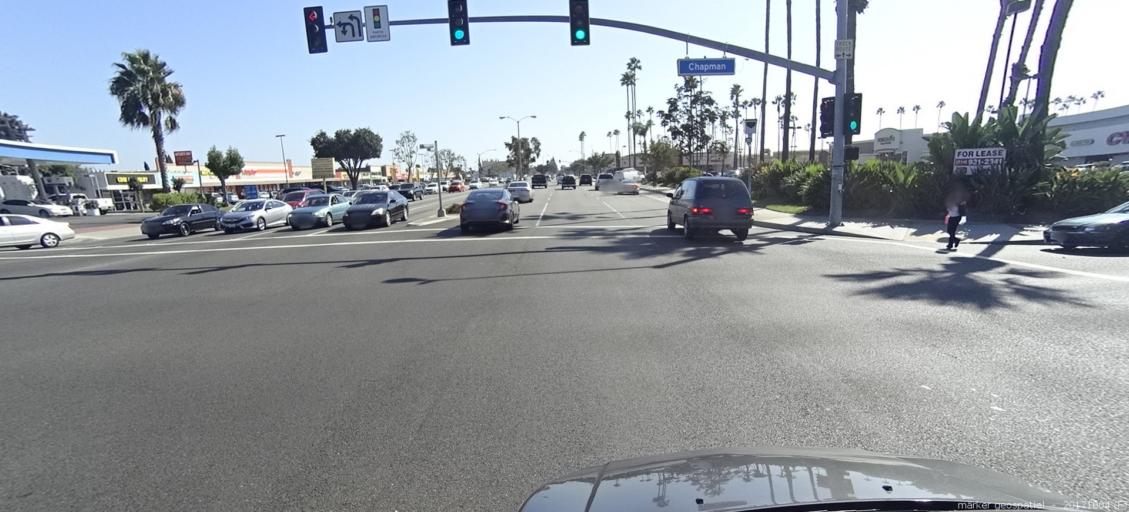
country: US
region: California
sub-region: Orange County
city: Garden Grove
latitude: 33.7886
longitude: -117.9588
